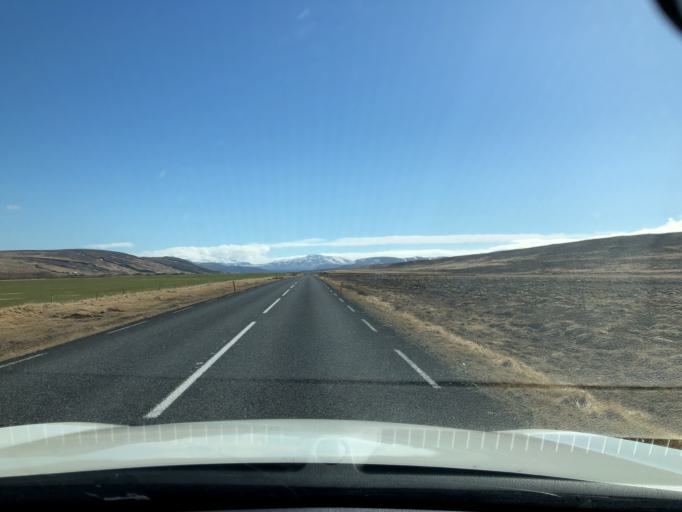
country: IS
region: South
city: Hveragerdi
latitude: 64.7015
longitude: -21.1895
